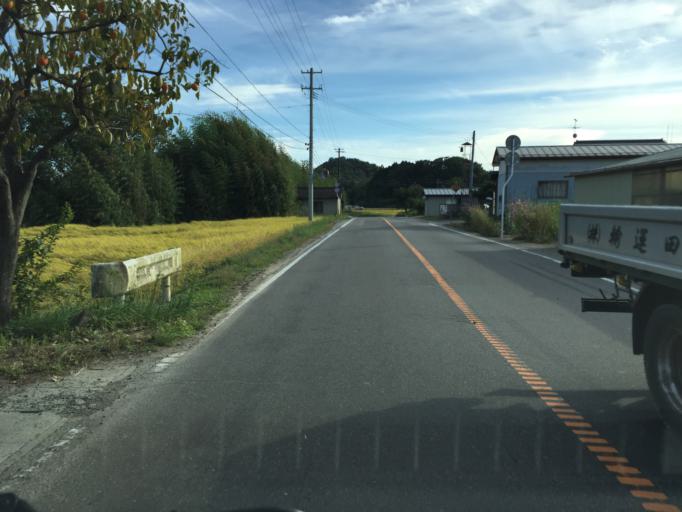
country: JP
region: Fukushima
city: Yanagawamachi-saiwaicho
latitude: 37.8437
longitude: 140.6150
